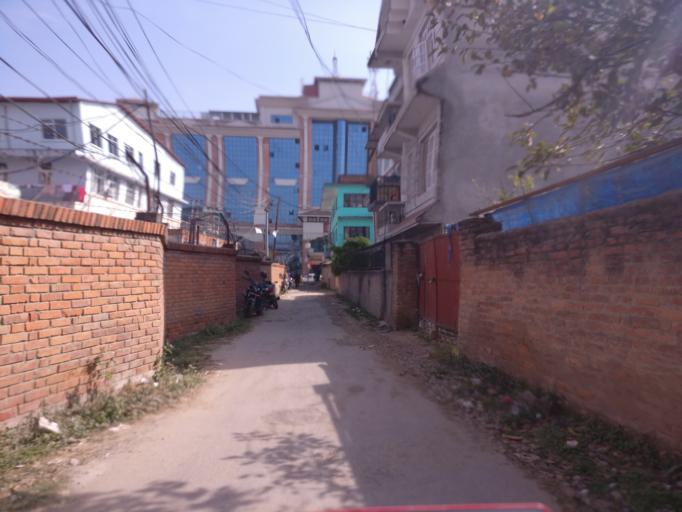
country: NP
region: Central Region
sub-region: Bagmati Zone
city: Patan
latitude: 27.6678
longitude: 85.3207
